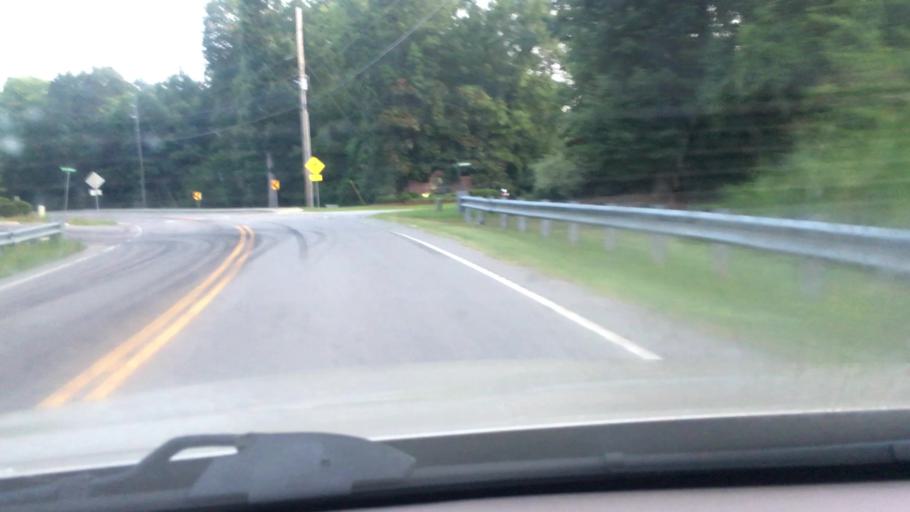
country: US
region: South Carolina
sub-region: Lexington County
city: Irmo
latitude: 34.1472
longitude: -81.1950
